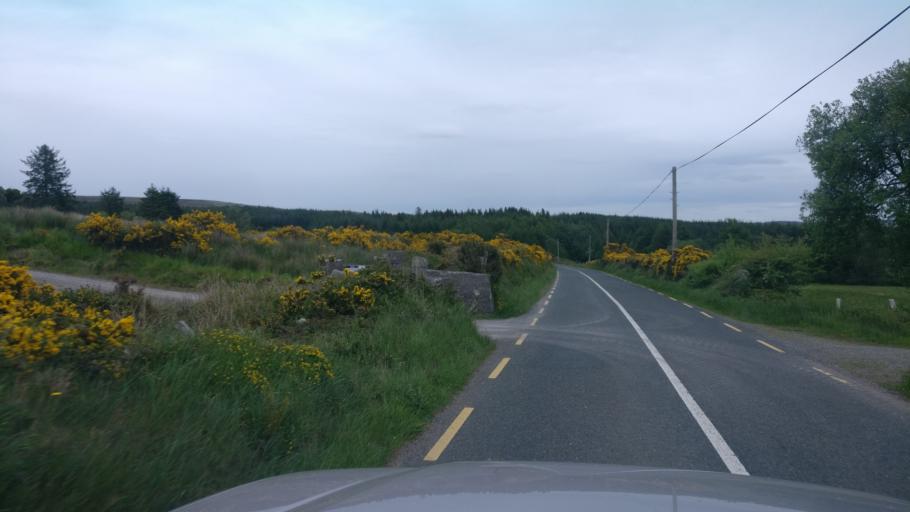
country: IE
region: Connaught
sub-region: County Galway
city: Gort
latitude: 53.0593
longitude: -8.6726
